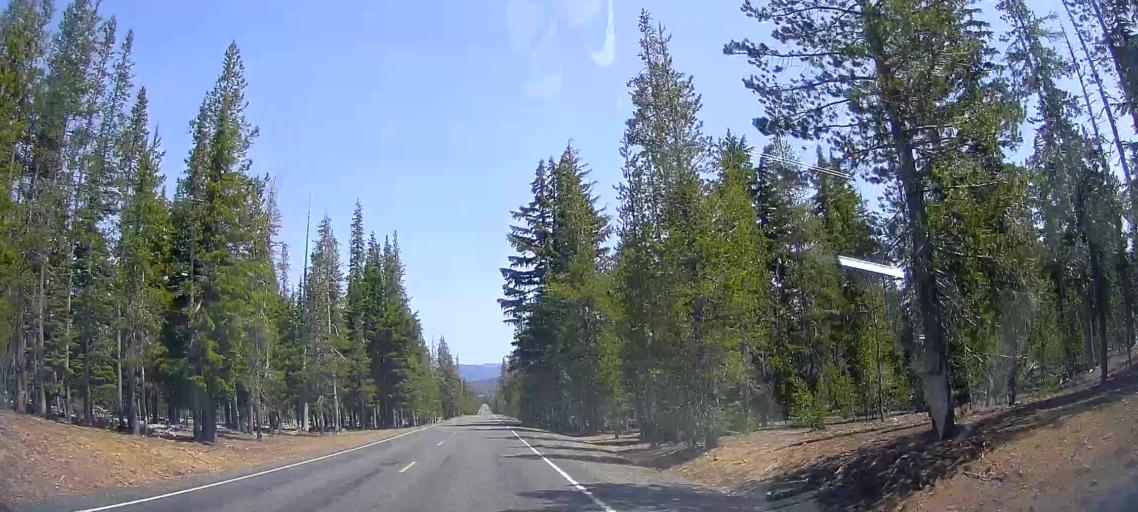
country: US
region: Oregon
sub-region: Jackson County
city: Shady Cove
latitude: 43.0135
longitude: -122.1283
